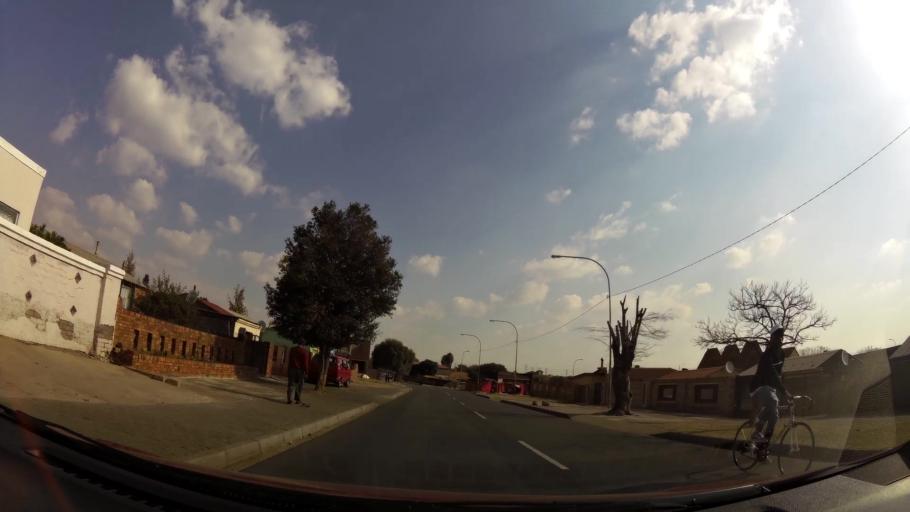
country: ZA
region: Gauteng
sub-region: City of Johannesburg Metropolitan Municipality
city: Soweto
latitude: -26.2379
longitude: 27.9444
